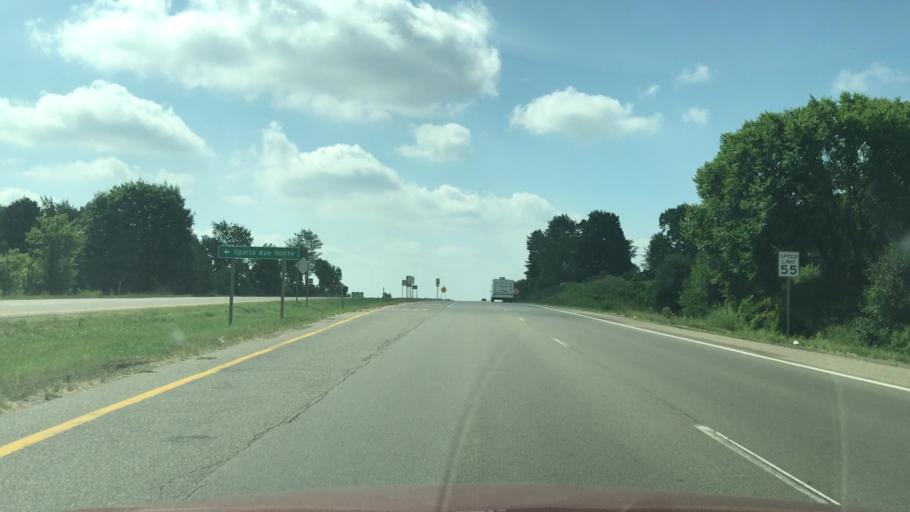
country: US
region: Michigan
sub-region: Kent County
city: Sparta
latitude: 43.1227
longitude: -85.7093
